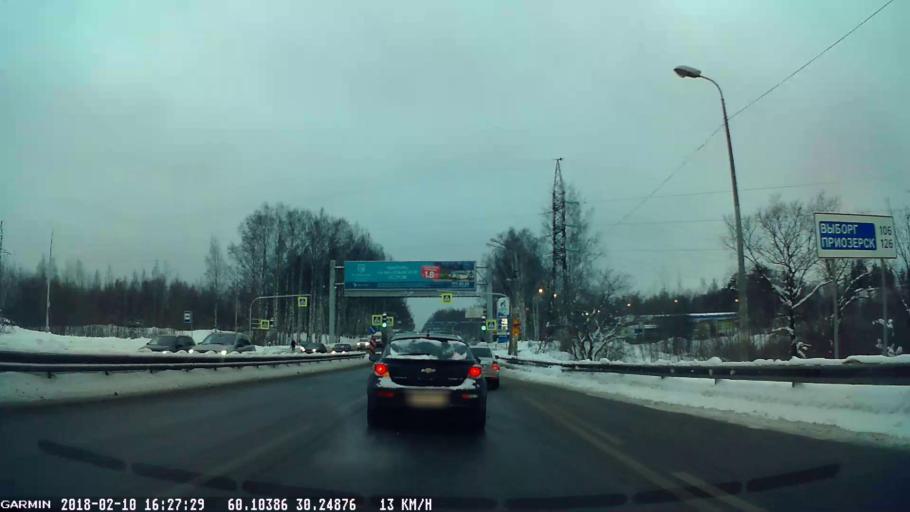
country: RU
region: St.-Petersburg
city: Pargolovo
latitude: 60.1039
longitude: 30.2487
